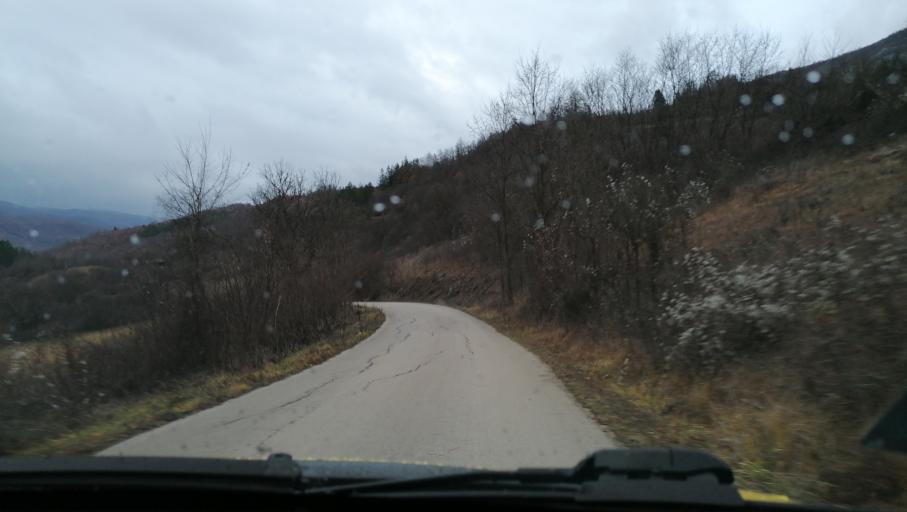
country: RS
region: Central Serbia
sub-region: Pirotski Okrug
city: Dimitrovgrad
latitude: 42.9764
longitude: 22.6554
